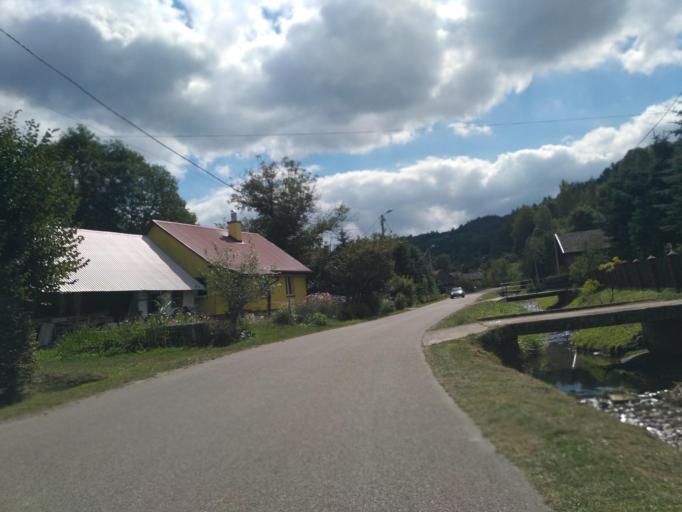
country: PL
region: Subcarpathian Voivodeship
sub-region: Powiat rzeszowski
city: Dynow
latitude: 49.7786
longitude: 22.2375
